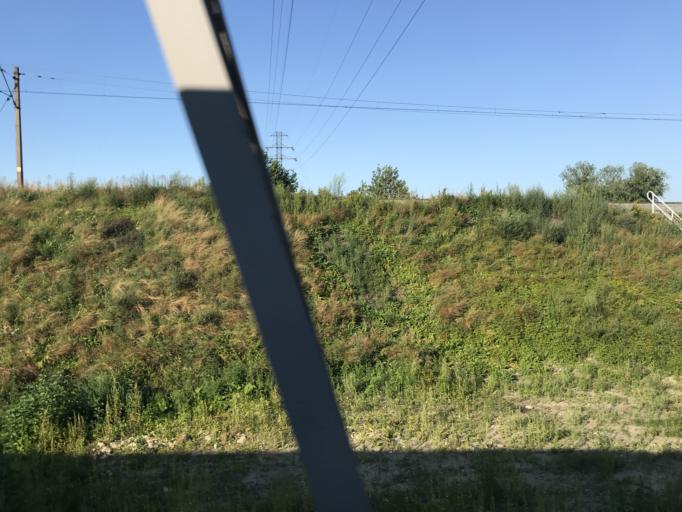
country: PL
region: Pomeranian Voivodeship
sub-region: Powiat tczewski
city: Tczew
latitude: 54.1085
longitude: 18.7796
